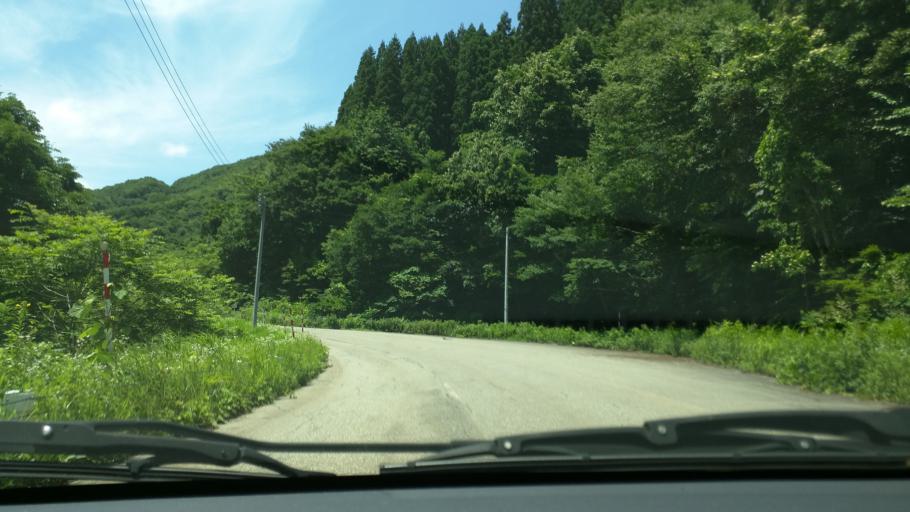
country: JP
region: Fukushima
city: Kitakata
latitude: 37.2577
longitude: 139.7541
